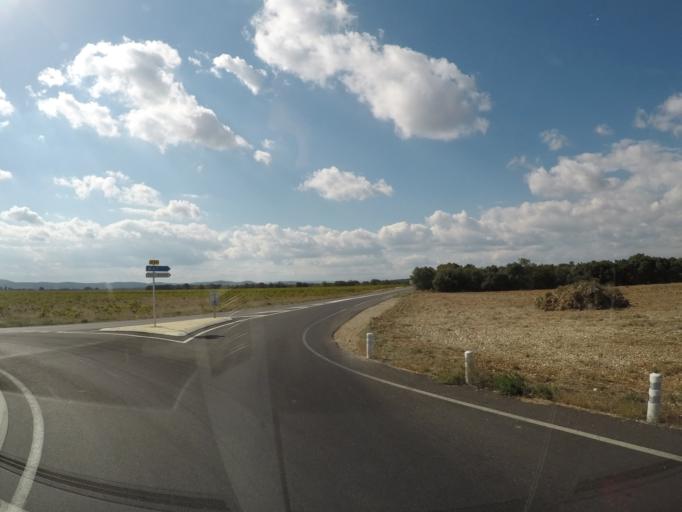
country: FR
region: Rhone-Alpes
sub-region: Departement de la Drome
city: Suze-la-Rousse
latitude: 44.2855
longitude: 4.8731
